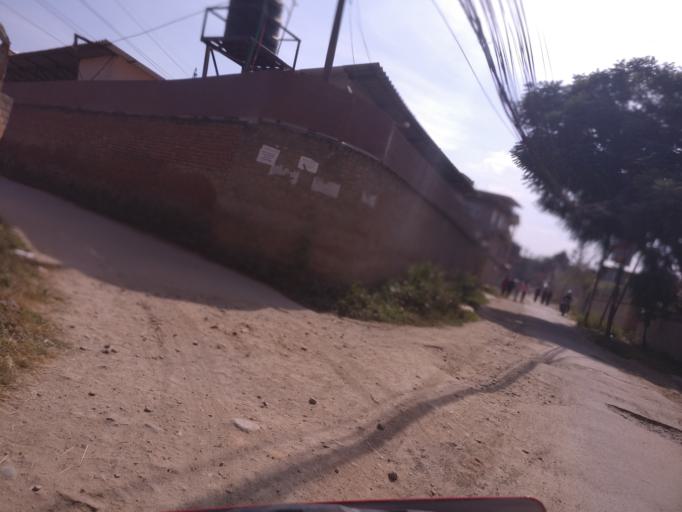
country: NP
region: Central Region
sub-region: Bagmati Zone
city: Patan
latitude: 27.6683
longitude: 85.3190
